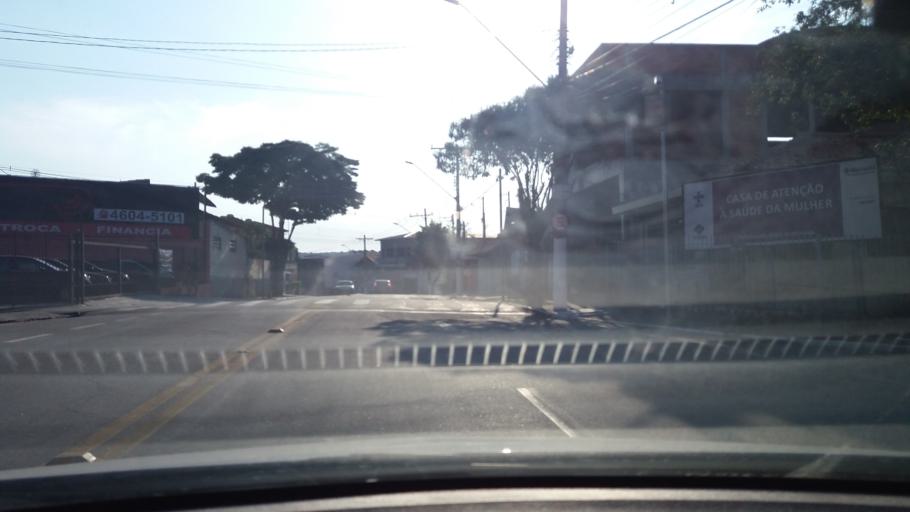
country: BR
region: Sao Paulo
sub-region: Mairipora
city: Mairipora
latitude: -23.3200
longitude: -46.5940
